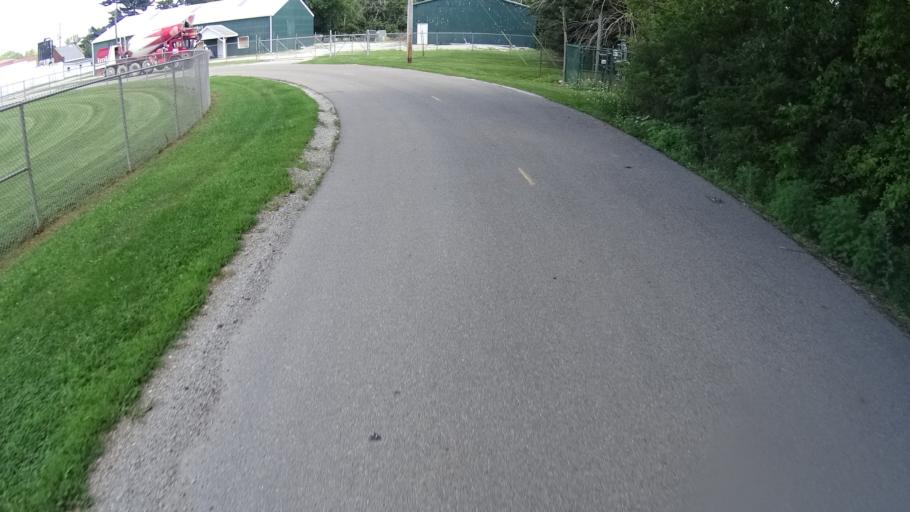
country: US
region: Indiana
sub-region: Madison County
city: Pendleton
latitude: 39.9988
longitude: -85.7385
